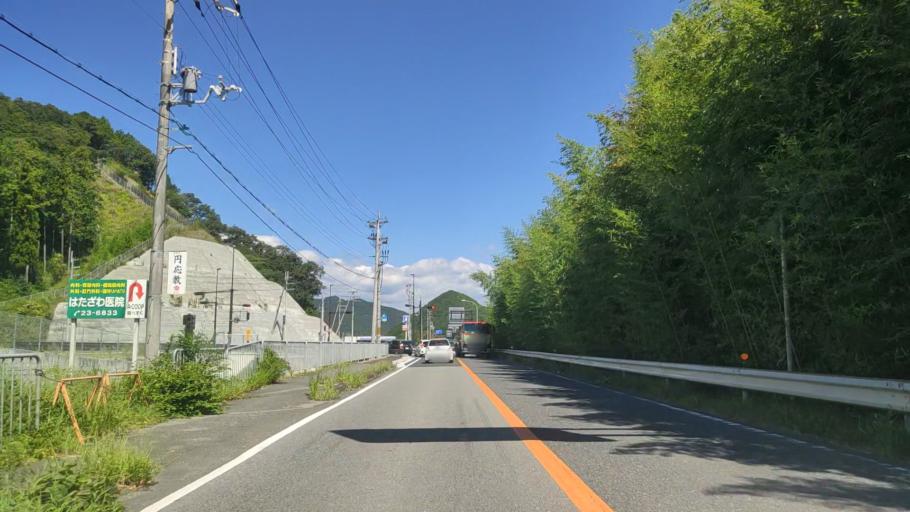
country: JP
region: Hyogo
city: Nishiwaki
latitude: 35.0218
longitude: 134.9837
